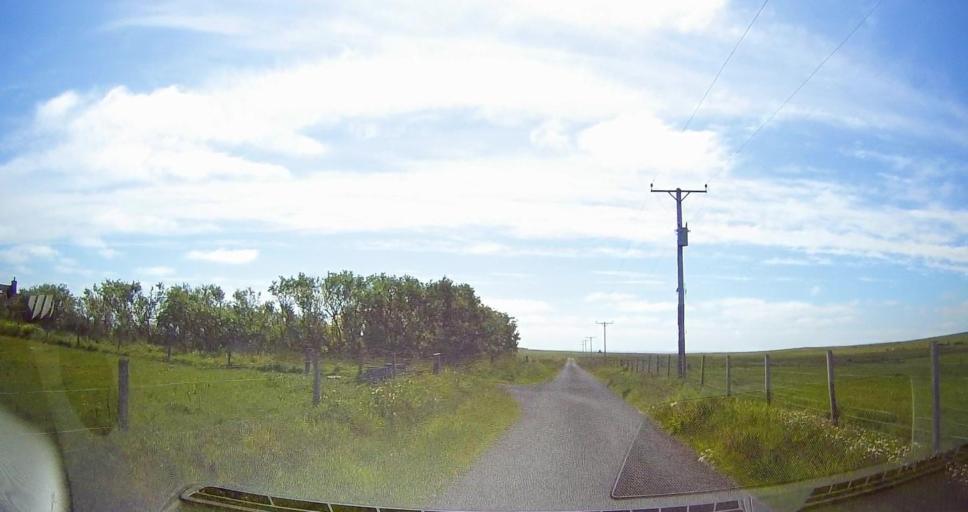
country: GB
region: Scotland
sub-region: Orkney Islands
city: Kirkwall
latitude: 58.8298
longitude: -2.8973
